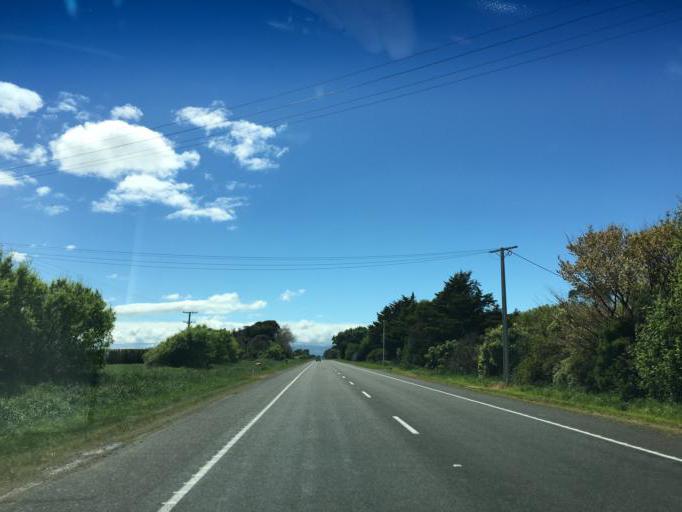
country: NZ
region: Manawatu-Wanganui
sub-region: Palmerston North City
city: Palmerston North
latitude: -40.4007
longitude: 175.5049
